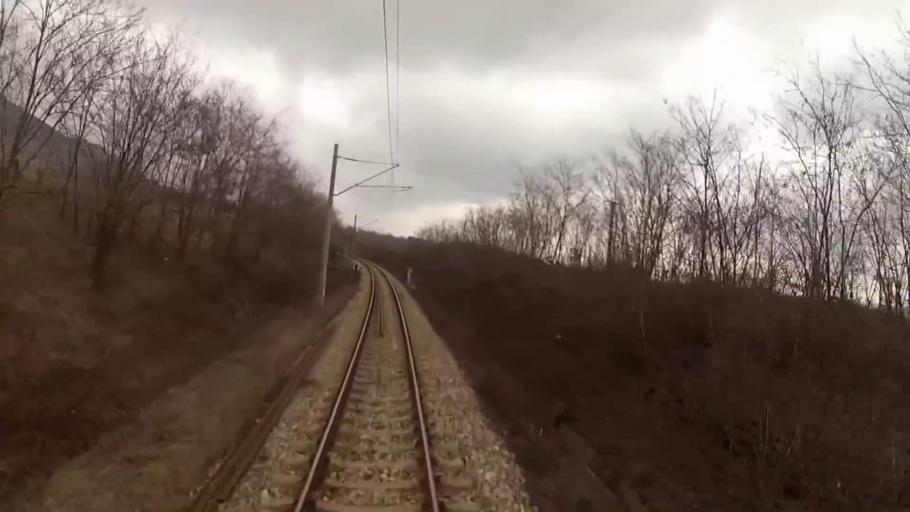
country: BG
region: Sofiya
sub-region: Obshtina Mirkovo
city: Mirkovo
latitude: 42.7035
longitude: 23.9574
